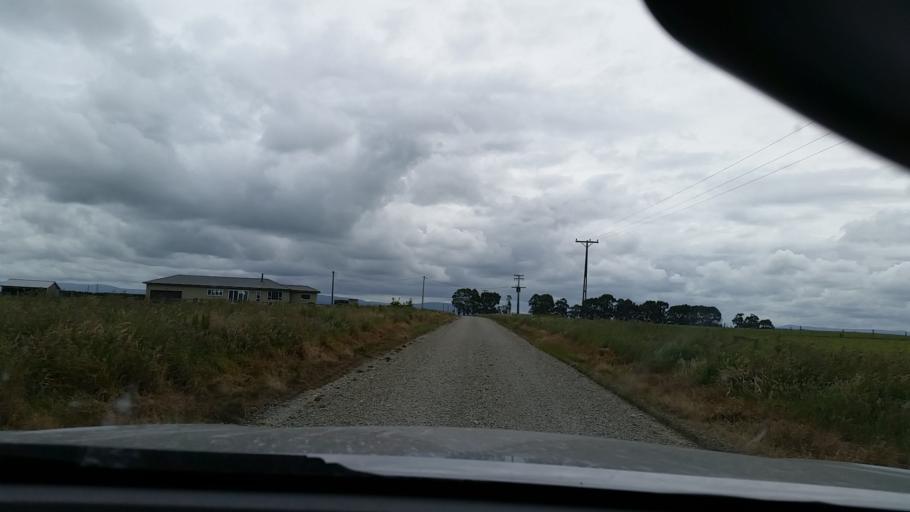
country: NZ
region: Southland
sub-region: Southland District
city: Winton
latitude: -46.1843
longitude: 168.2091
